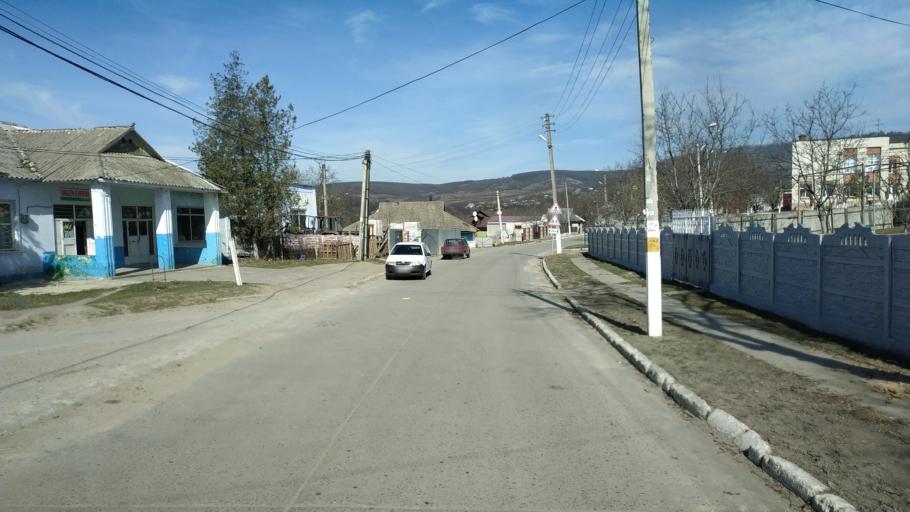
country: MD
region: Nisporeni
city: Nisporeni
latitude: 47.0750
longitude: 28.2606
